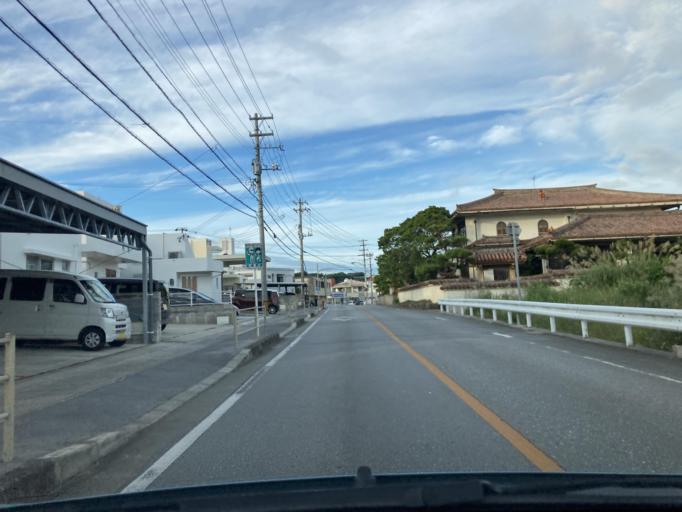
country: JP
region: Okinawa
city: Itoman
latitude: 26.1424
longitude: 127.6889
